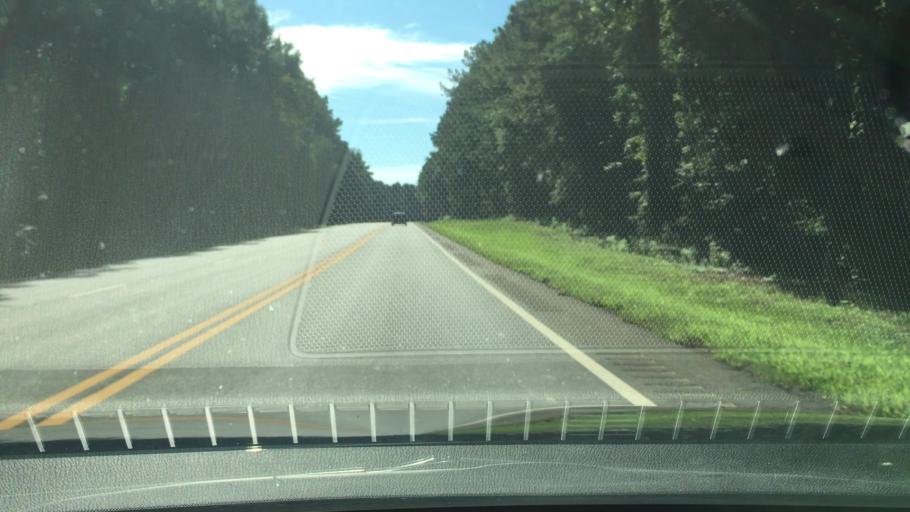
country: US
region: Georgia
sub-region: Putnam County
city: Jefferson
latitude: 33.4368
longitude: -83.3835
